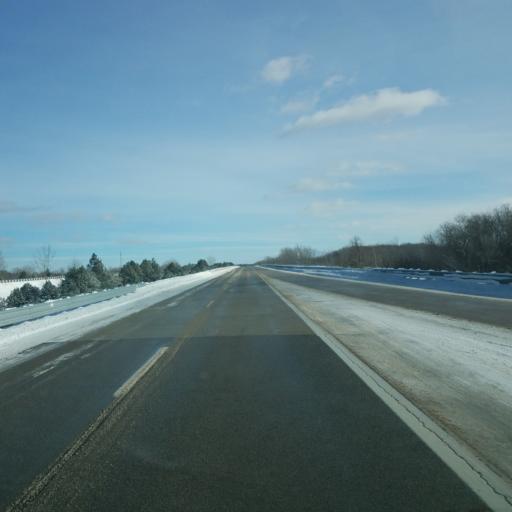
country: US
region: Michigan
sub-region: Clare County
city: Clare
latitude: 43.8643
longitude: -84.9109
